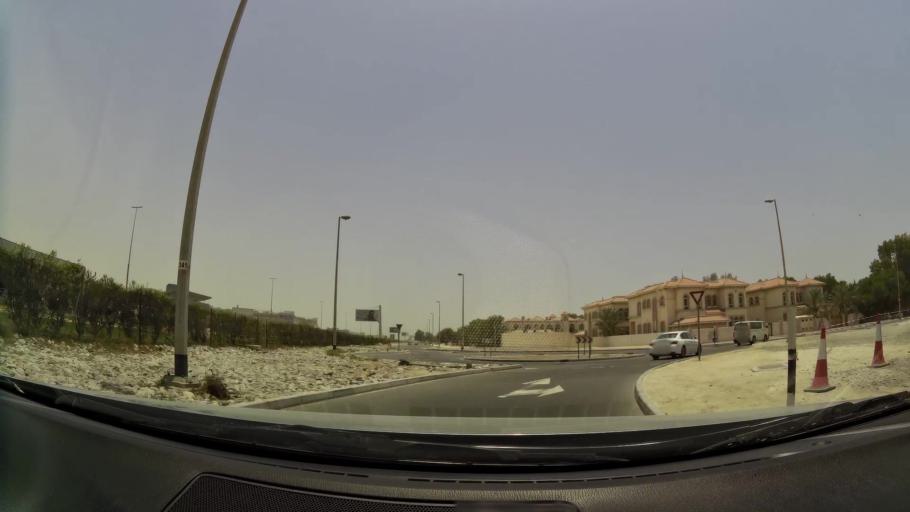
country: AE
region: Dubai
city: Dubai
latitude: 25.1756
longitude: 55.2443
